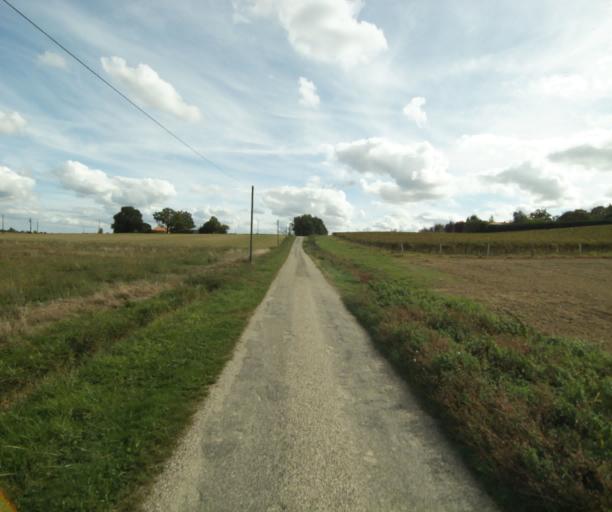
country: FR
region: Midi-Pyrenees
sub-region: Departement du Gers
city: Eauze
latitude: 43.8326
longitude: 0.1667
